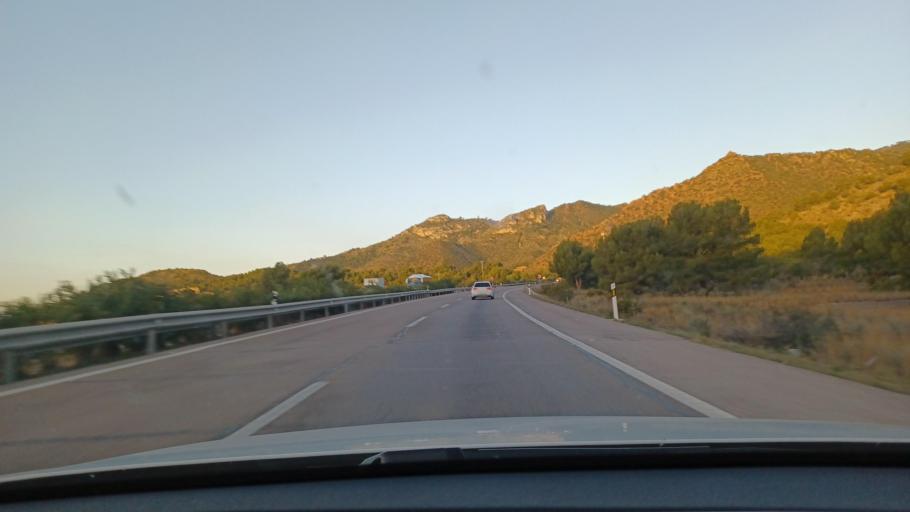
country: ES
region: Valencia
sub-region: Provincia de Castello
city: Benicassim
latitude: 40.0617
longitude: 0.0616
